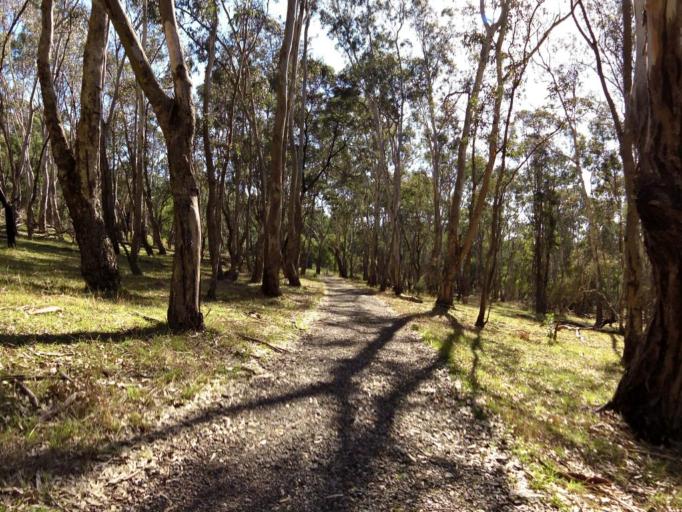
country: AU
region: Victoria
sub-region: Yarra Ranges
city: Lysterfield
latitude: -37.9496
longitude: 145.2855
